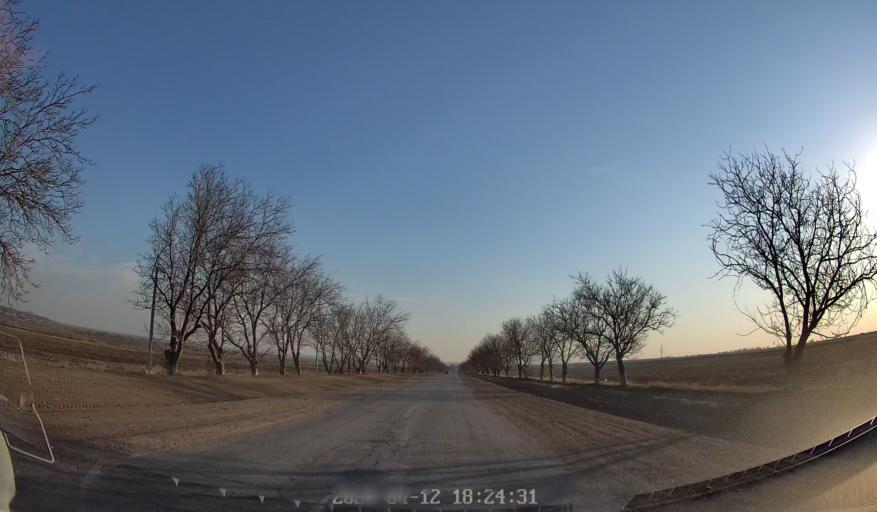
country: MD
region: Criuleni
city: Criuleni
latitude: 47.1951
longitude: 29.1496
